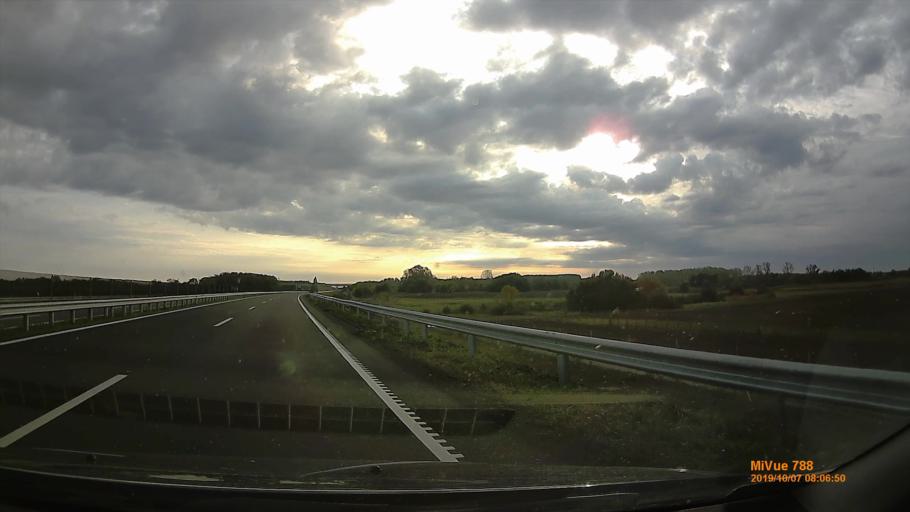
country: HU
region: Jasz-Nagykun-Szolnok
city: Cserkeszolo
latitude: 46.8854
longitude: 20.1809
